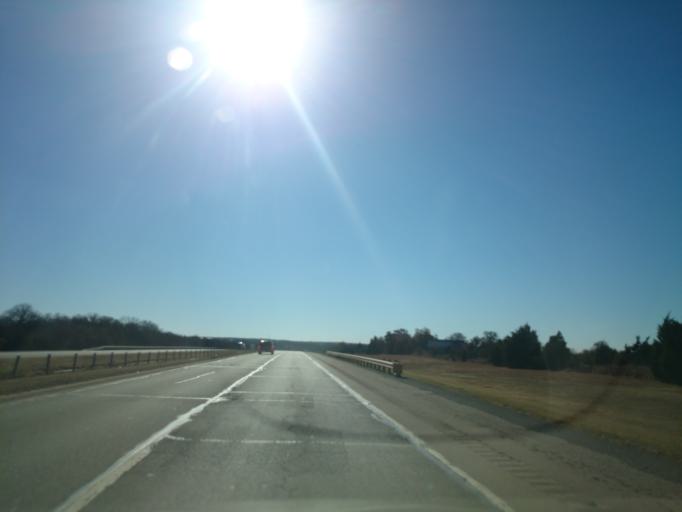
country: US
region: Oklahoma
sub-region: Logan County
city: Guthrie
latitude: 35.8503
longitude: -97.3944
